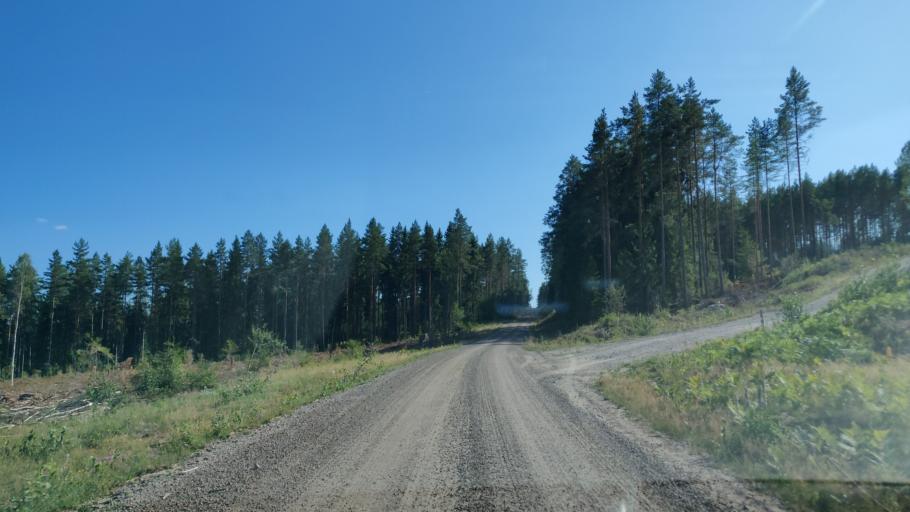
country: SE
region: Vaermland
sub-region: Hagfors Kommun
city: Ekshaerad
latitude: 60.1463
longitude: 13.5163
